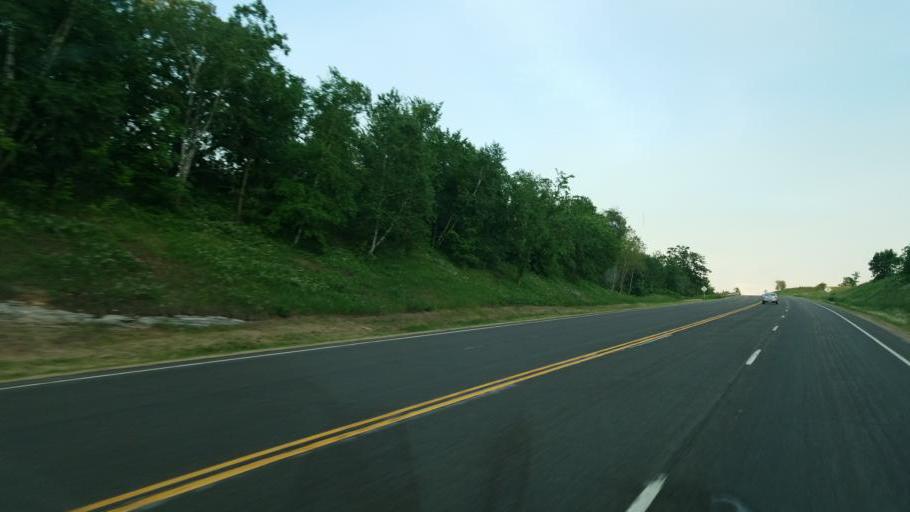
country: US
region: Wisconsin
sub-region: Monroe County
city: Tomah
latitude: 43.9053
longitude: -90.4926
